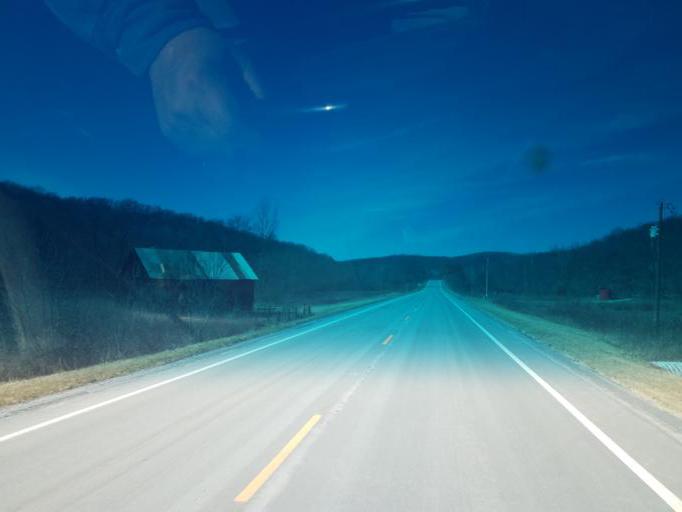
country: US
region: Ohio
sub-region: Knox County
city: Oak Hill
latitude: 40.4630
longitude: -82.1780
